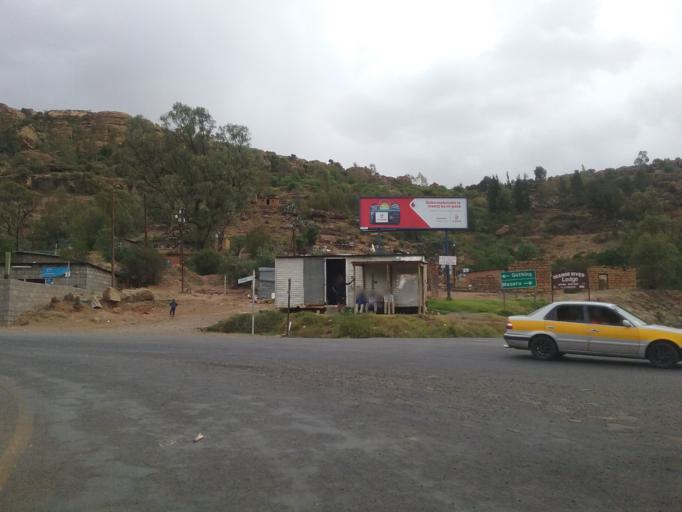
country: LS
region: Quthing
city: Quthing
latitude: -30.3983
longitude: 27.6909
